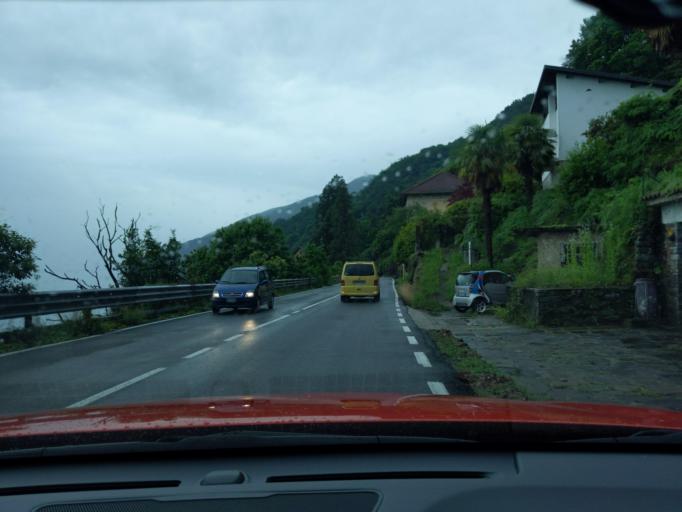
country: IT
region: Piedmont
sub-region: Provincia Verbano-Cusio-Ossola
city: Cannobio
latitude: 46.0910
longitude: 8.6915
